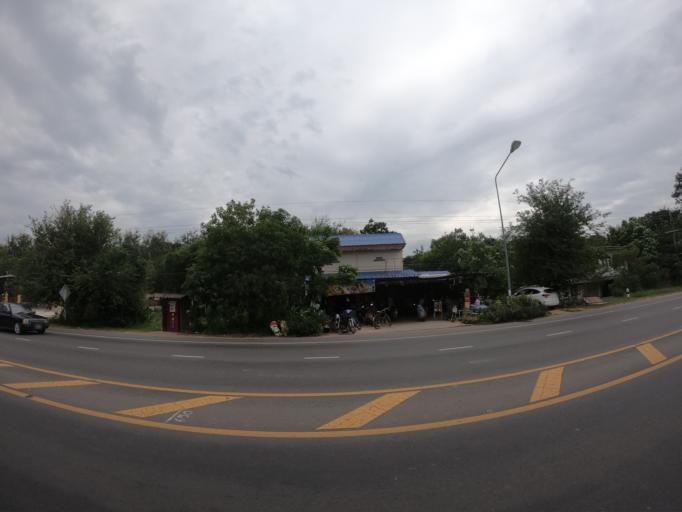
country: TH
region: Roi Et
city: Thawat Buri
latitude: 16.0835
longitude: 103.7448
